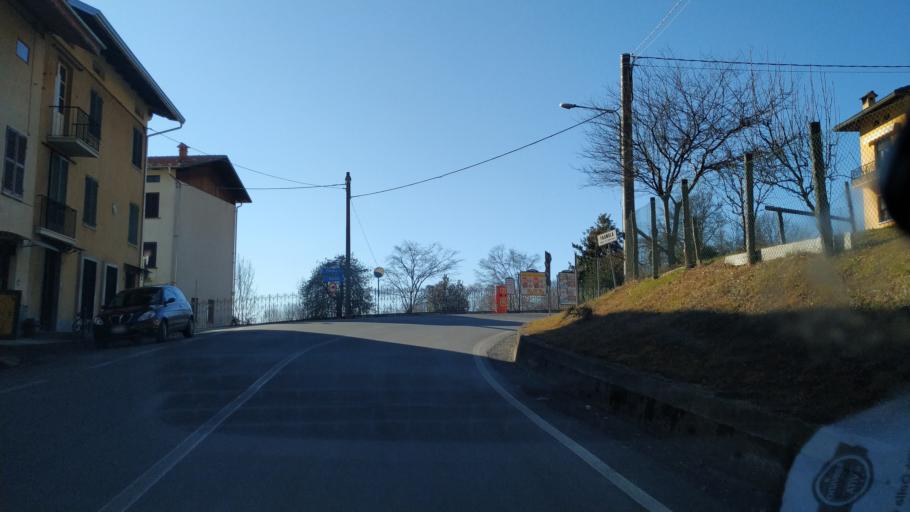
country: IT
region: Piedmont
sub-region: Provincia di Biella
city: Portula
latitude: 45.6757
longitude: 8.1768
